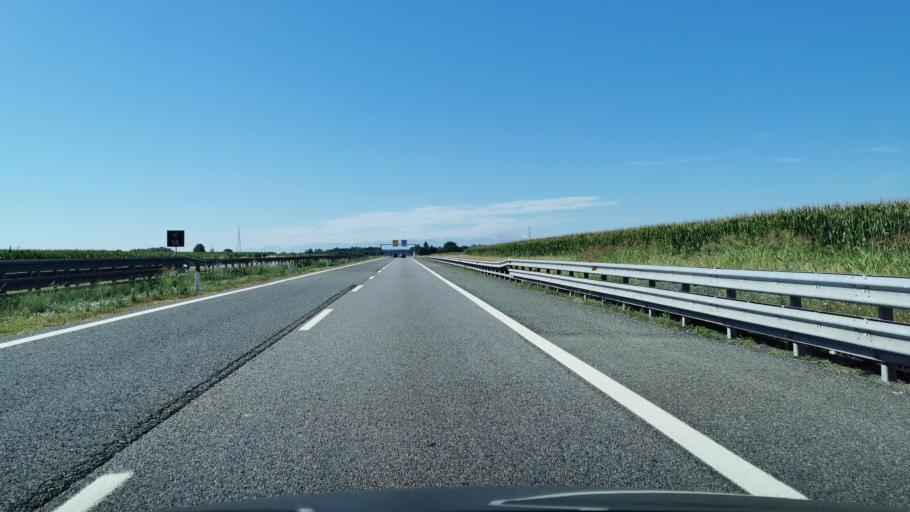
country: IT
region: Piedmont
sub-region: Provincia di Torino
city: Carmagnola
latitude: 44.8695
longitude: 7.7478
